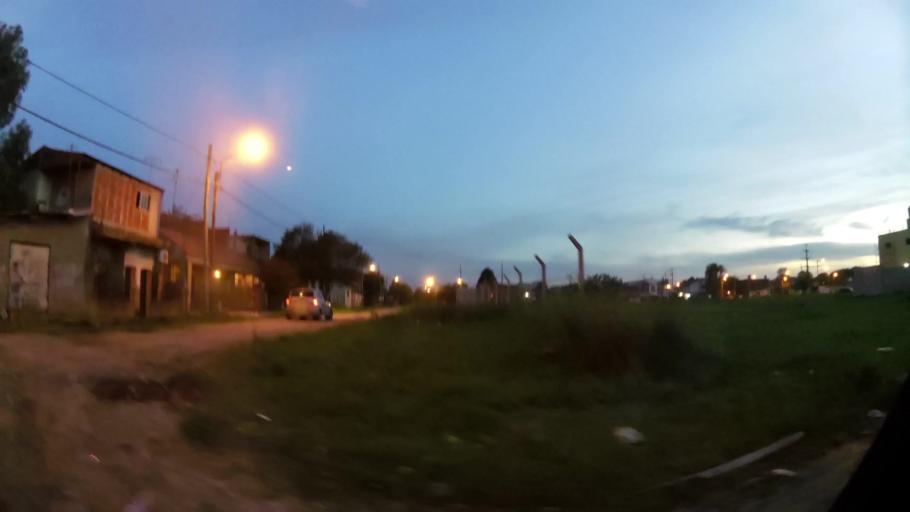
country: AR
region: Buenos Aires
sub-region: Partido de Almirante Brown
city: Adrogue
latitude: -34.8055
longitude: -58.2952
